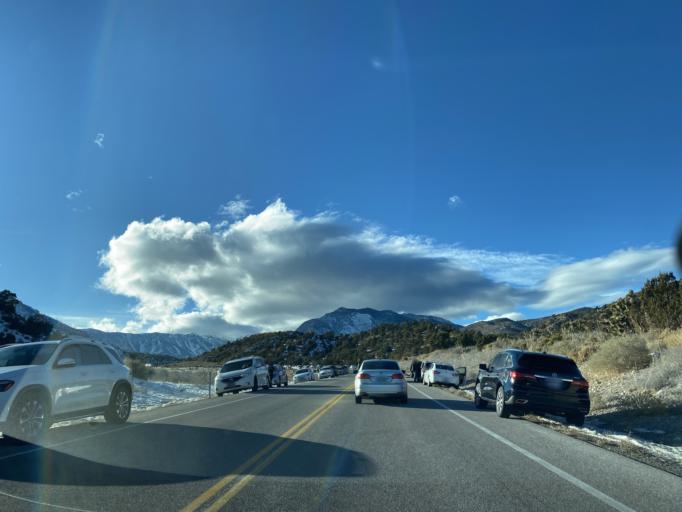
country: US
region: Nevada
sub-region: Clark County
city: Summerlin South
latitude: 36.2718
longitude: -115.5368
